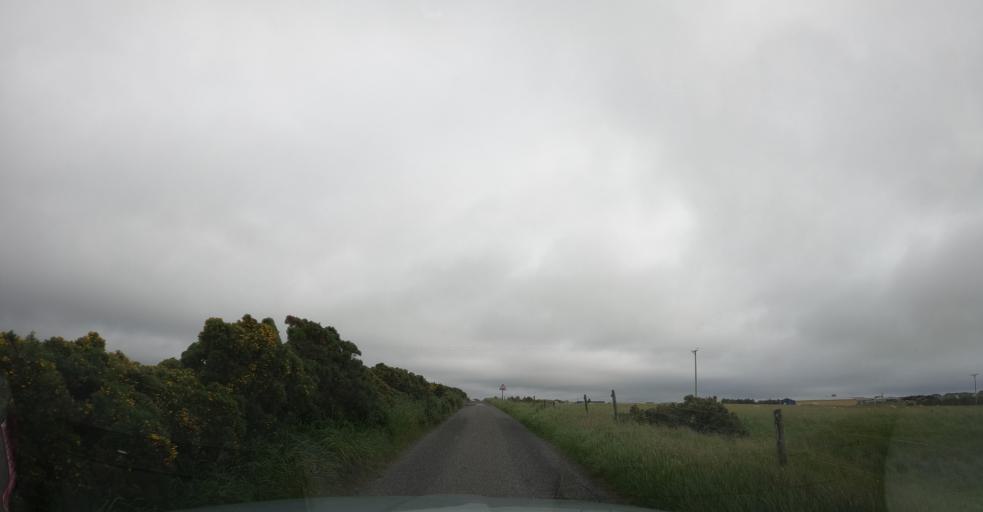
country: GB
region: Scotland
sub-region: Eilean Siar
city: Stornoway
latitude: 58.1984
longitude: -6.3494
